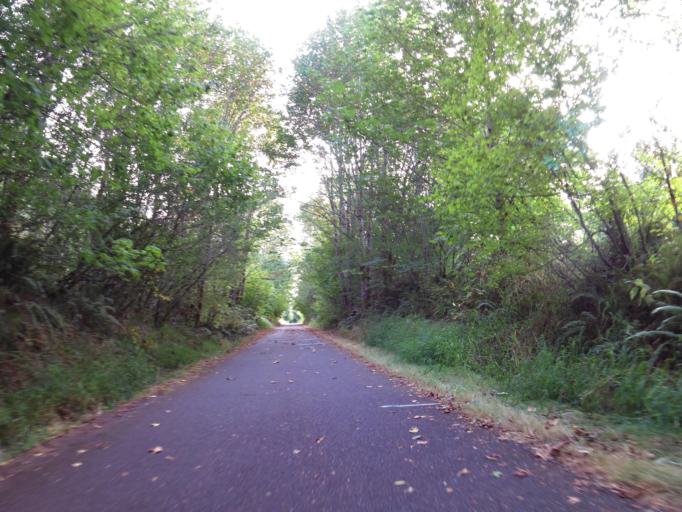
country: US
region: Washington
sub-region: Thurston County
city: Lacey
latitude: 46.9472
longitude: -122.8164
